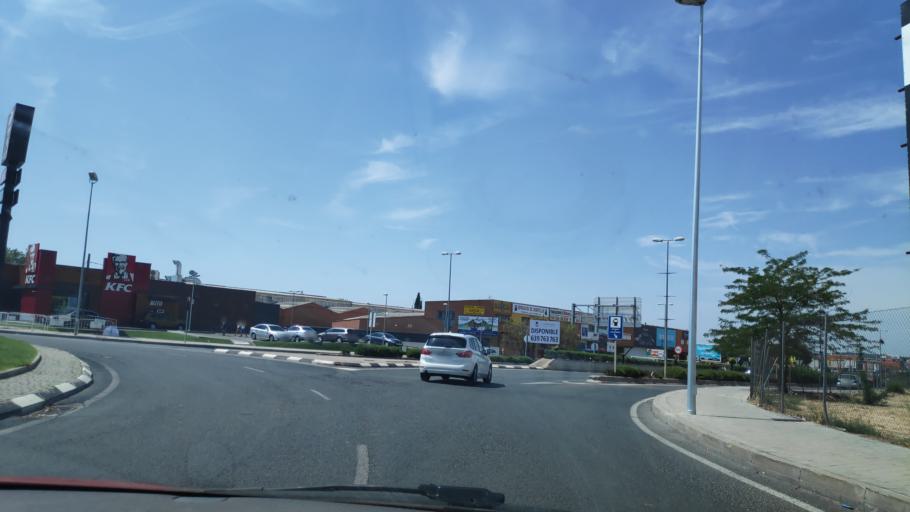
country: ES
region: Madrid
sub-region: Provincia de Madrid
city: Arganda
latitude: 40.3090
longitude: -3.4750
